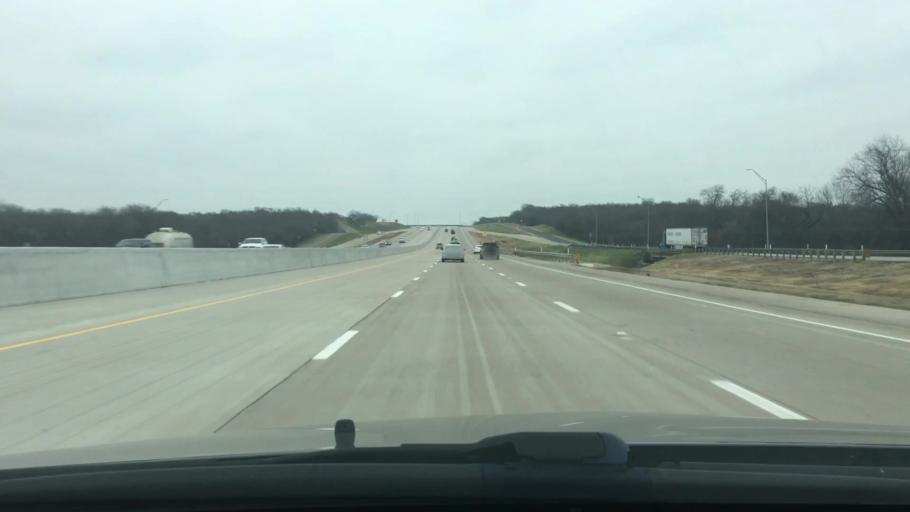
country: US
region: Texas
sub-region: Freestone County
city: Wortham
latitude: 31.9101
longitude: -96.3926
